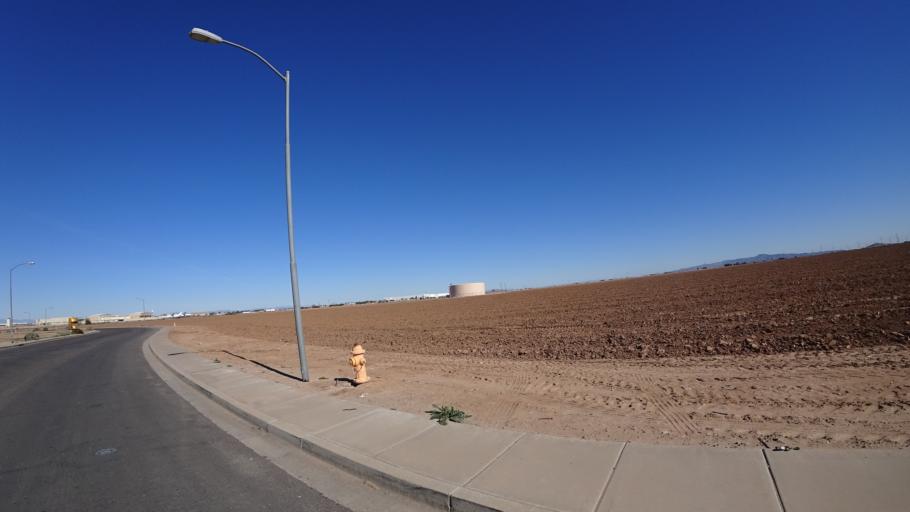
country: US
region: Arizona
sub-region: Maricopa County
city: Goodyear
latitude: 33.4147
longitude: -112.3705
